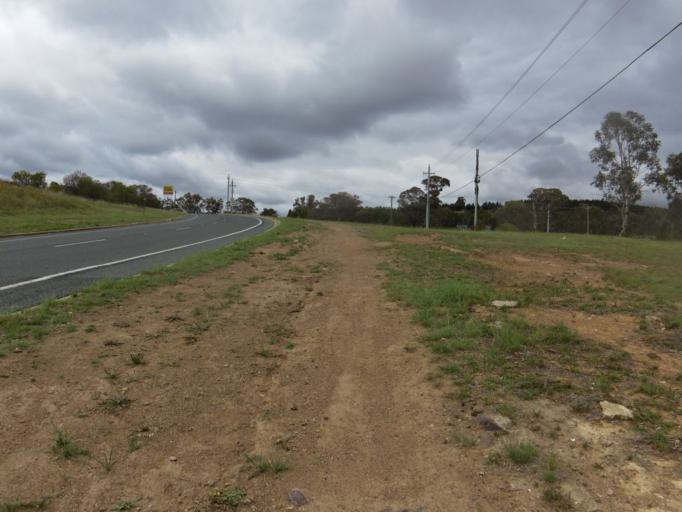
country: AU
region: Australian Capital Territory
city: Macquarie
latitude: -35.3299
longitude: 149.0260
